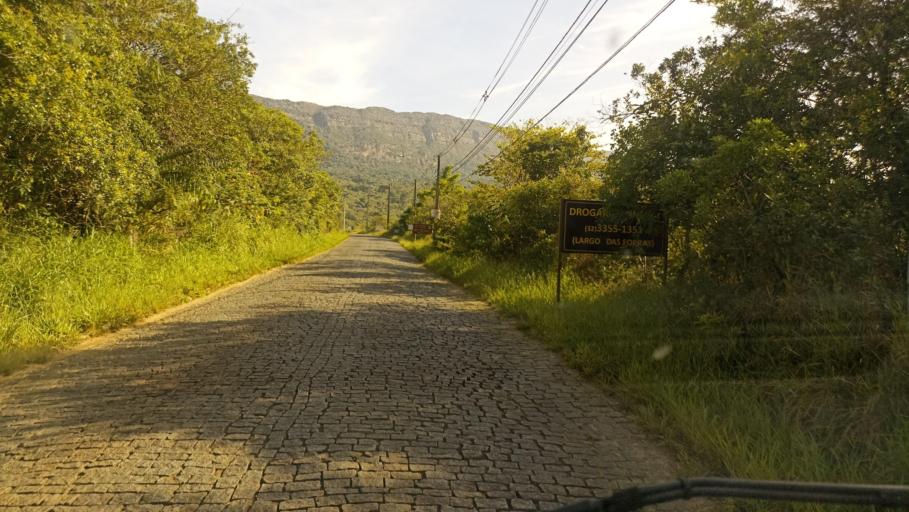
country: BR
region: Minas Gerais
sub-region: Tiradentes
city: Tiradentes
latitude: -21.1178
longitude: -44.1896
